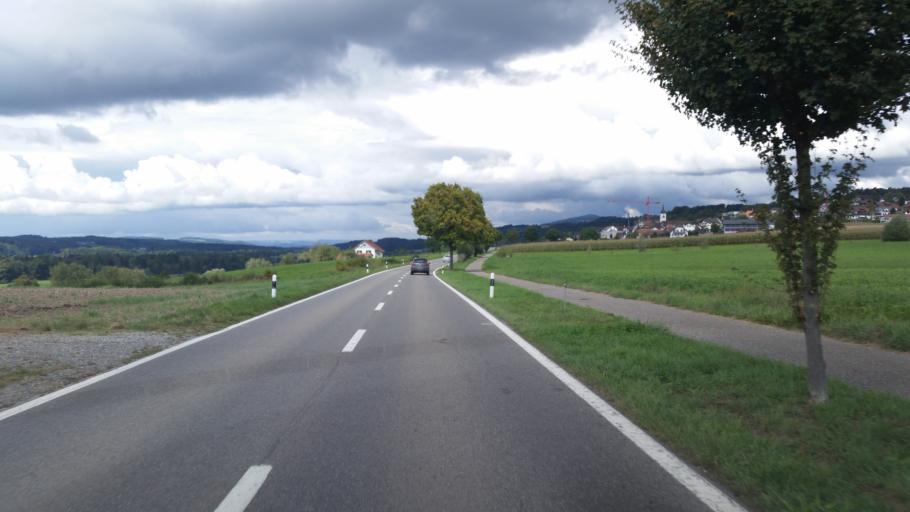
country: CH
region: Aargau
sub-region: Bezirk Bremgarten
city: Jonen
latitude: 47.3035
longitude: 8.3919
